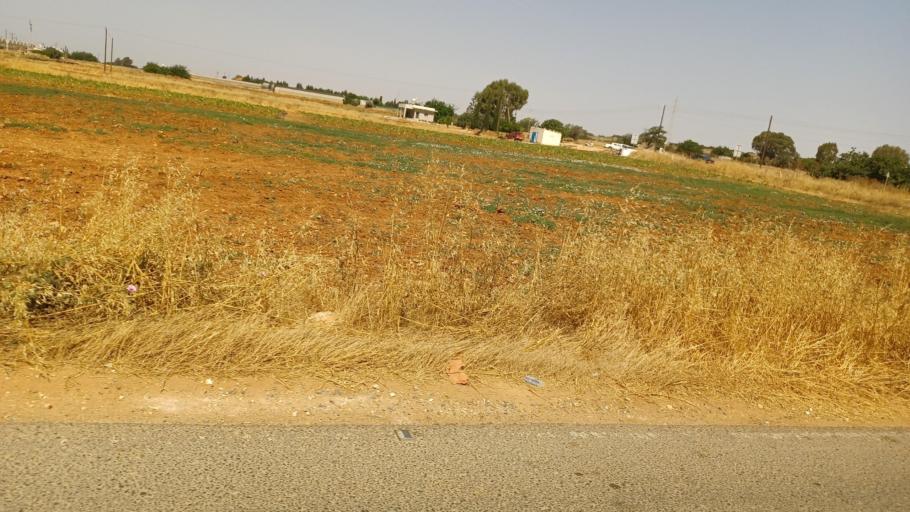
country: CY
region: Ammochostos
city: Paralimni
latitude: 35.0002
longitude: 33.9510
